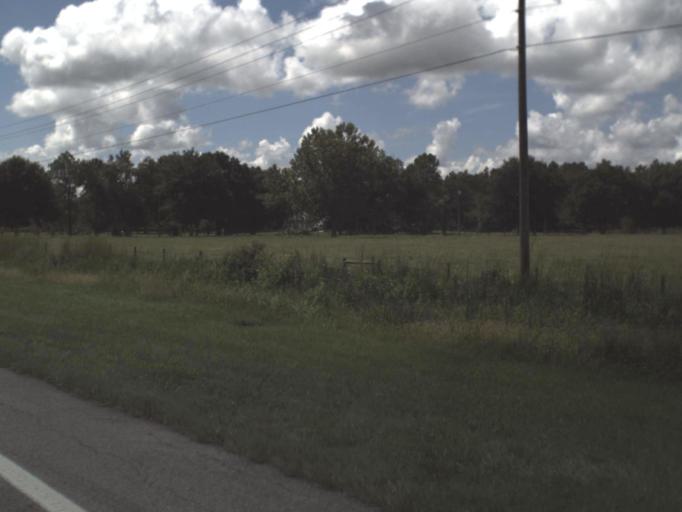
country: US
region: Florida
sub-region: Polk County
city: Polk City
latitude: 28.2563
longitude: -81.8238
